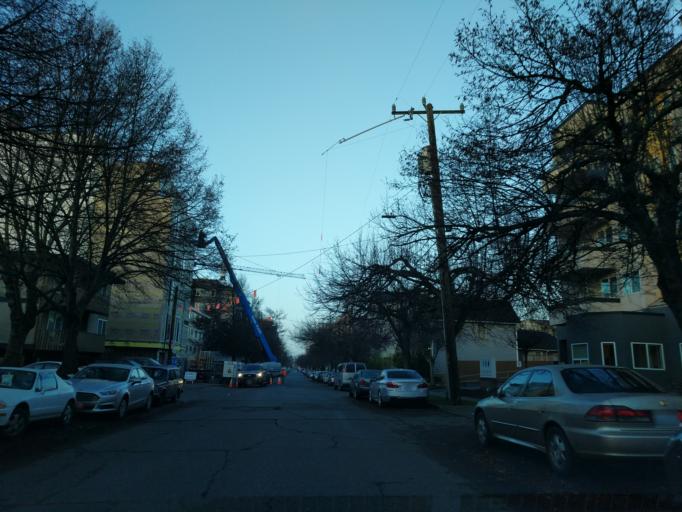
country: US
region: Washington
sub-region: King County
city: Seattle
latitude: 47.6702
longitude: -122.3794
